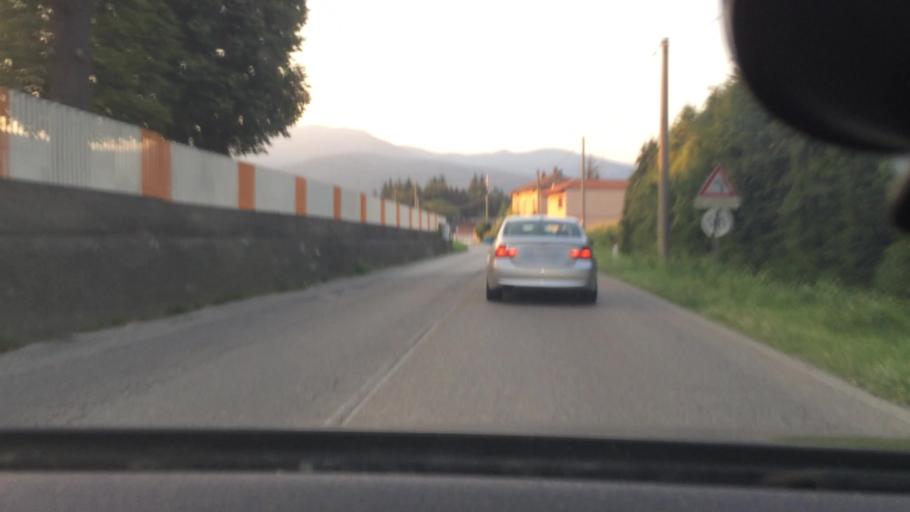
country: IT
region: Lombardy
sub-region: Provincia di Como
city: Anzano del Parco
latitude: 45.7755
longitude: 9.1939
